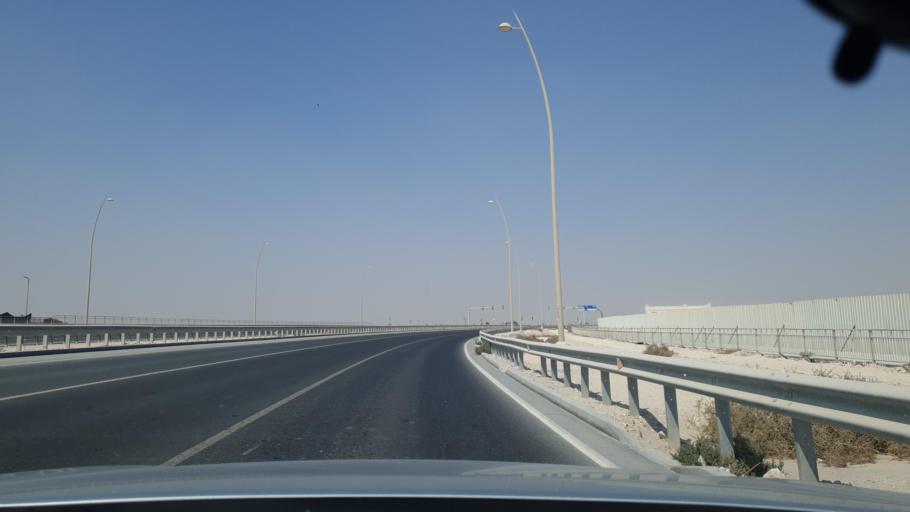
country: QA
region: Al Khawr
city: Al Khawr
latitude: 25.6612
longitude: 51.4802
